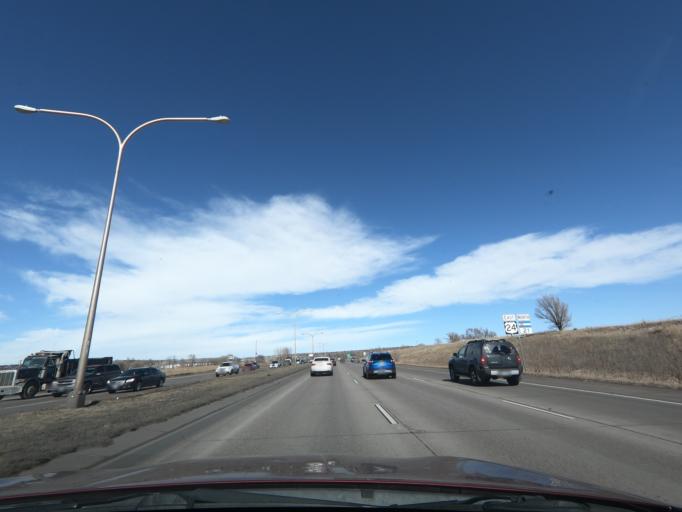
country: US
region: Colorado
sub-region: El Paso County
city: Cimarron Hills
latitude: 38.8270
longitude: -104.7234
